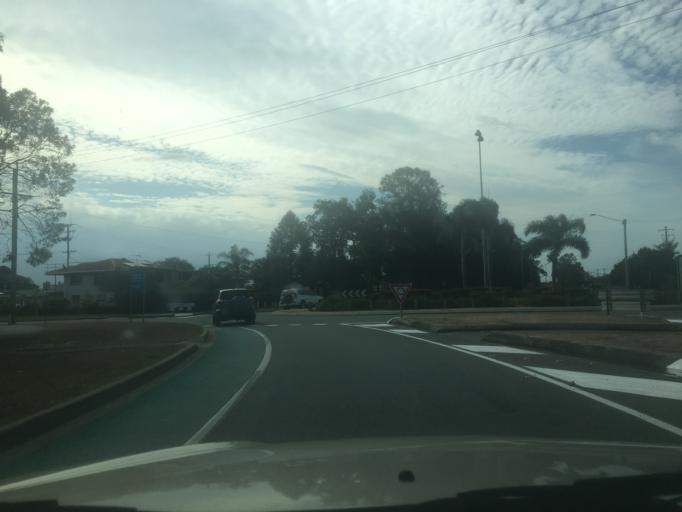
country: AU
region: Queensland
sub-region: Moreton Bay
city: Bongaree
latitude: -27.0766
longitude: 153.1647
